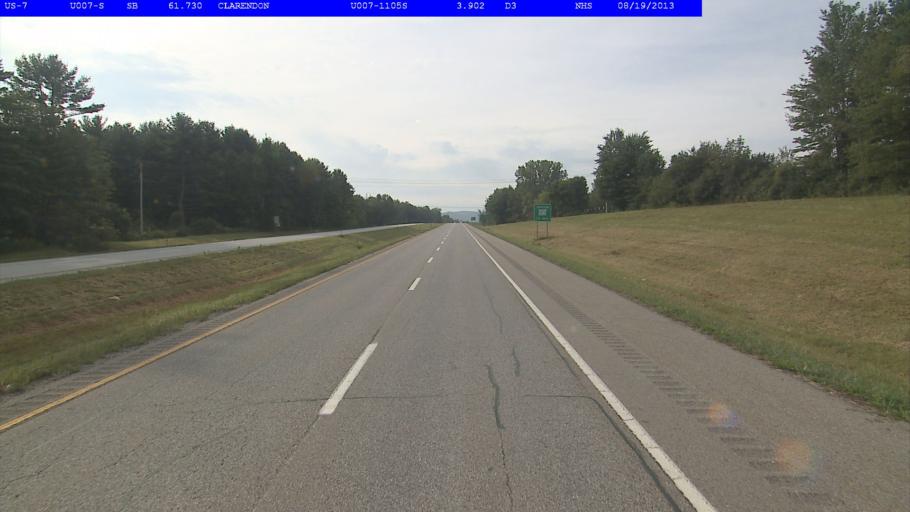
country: US
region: Vermont
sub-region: Rutland County
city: Rutland
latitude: 43.5485
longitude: -72.9619
